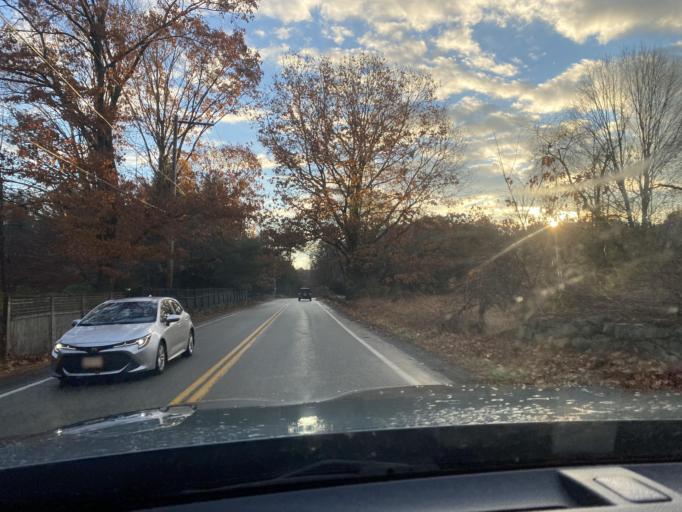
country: US
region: Massachusetts
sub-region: Norfolk County
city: Dover
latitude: 42.2536
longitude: -71.2568
